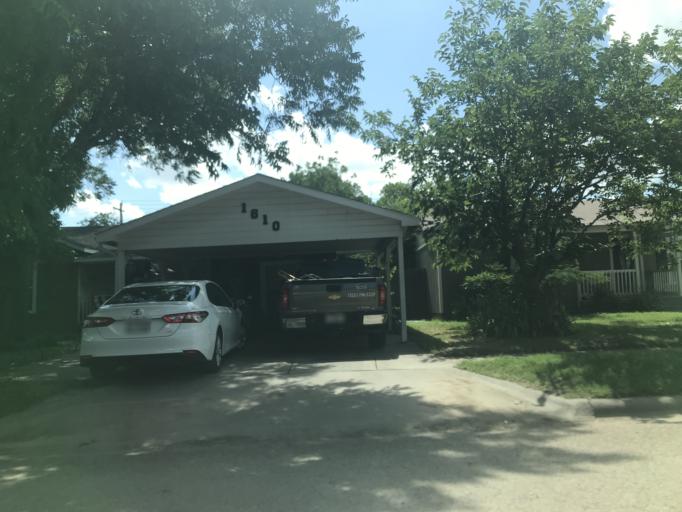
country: US
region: Texas
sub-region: Taylor County
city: Abilene
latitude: 32.4295
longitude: -99.7624
